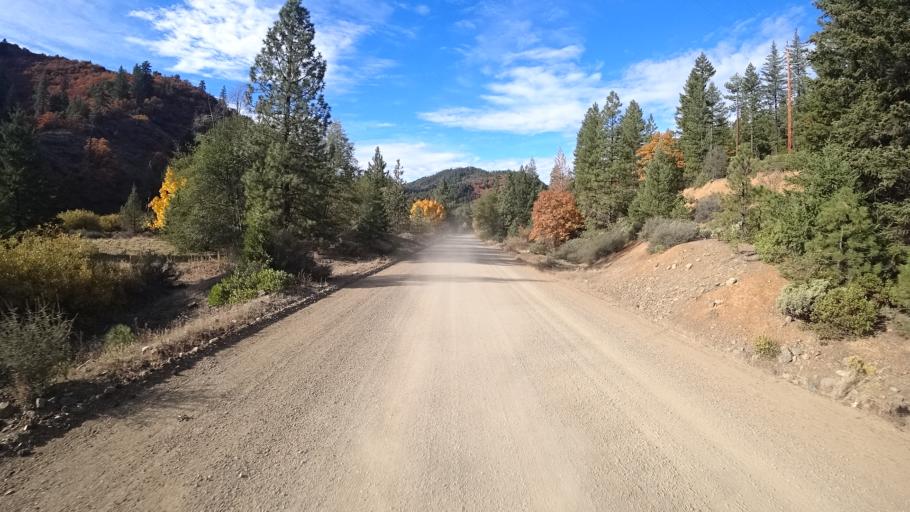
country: US
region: California
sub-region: Siskiyou County
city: Yreka
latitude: 41.7120
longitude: -122.8067
